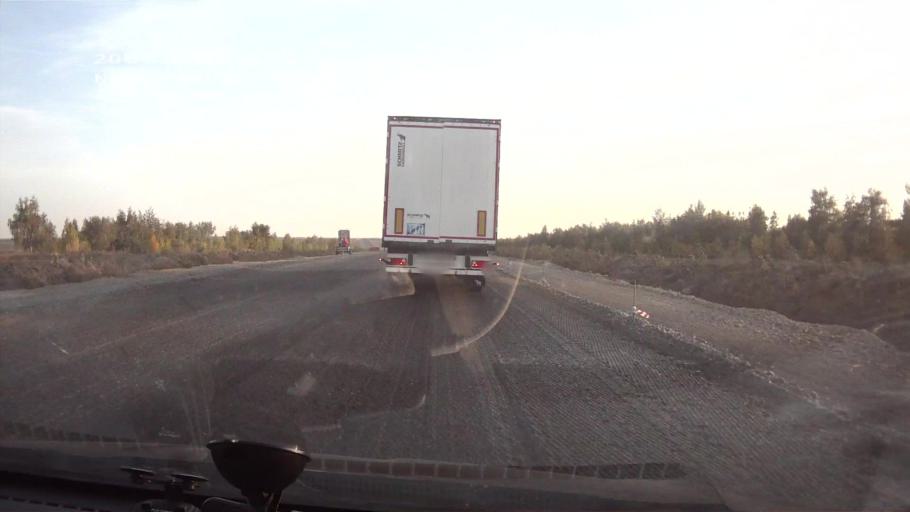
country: RU
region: Saratov
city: Krasnoarmeysk
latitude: 51.0004
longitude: 45.6140
